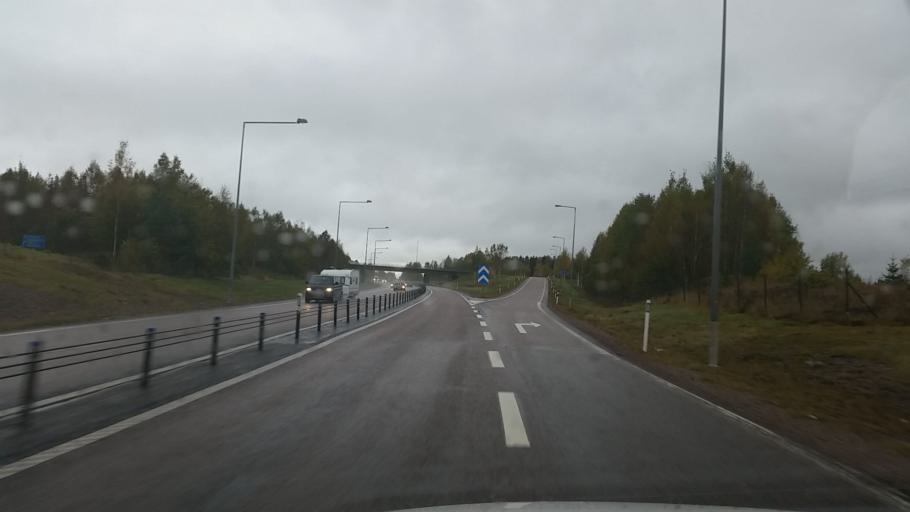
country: SE
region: Gaevleborg
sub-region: Sandvikens Kommun
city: Jarbo
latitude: 60.6060
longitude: 16.5919
